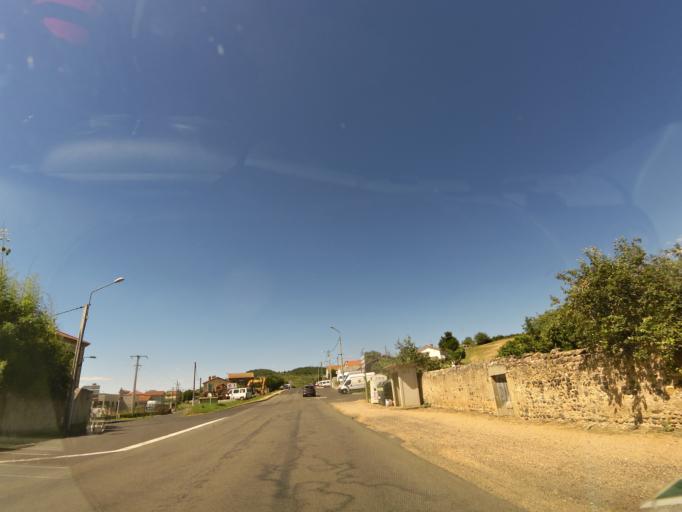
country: FR
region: Auvergne
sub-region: Departement du Puy-de-Dome
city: Saint-Germain-Lembron
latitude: 45.4643
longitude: 3.2369
